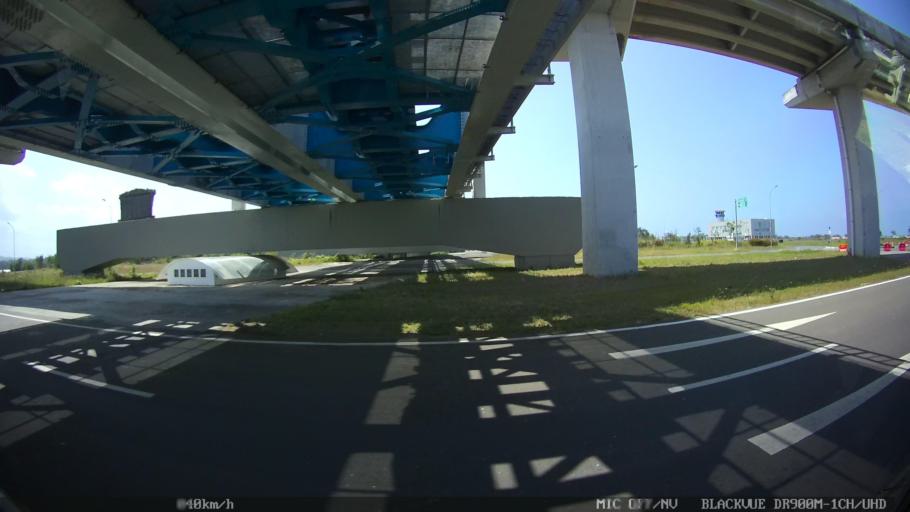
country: ID
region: Daerah Istimewa Yogyakarta
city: Srandakan
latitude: -7.8979
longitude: 110.0632
